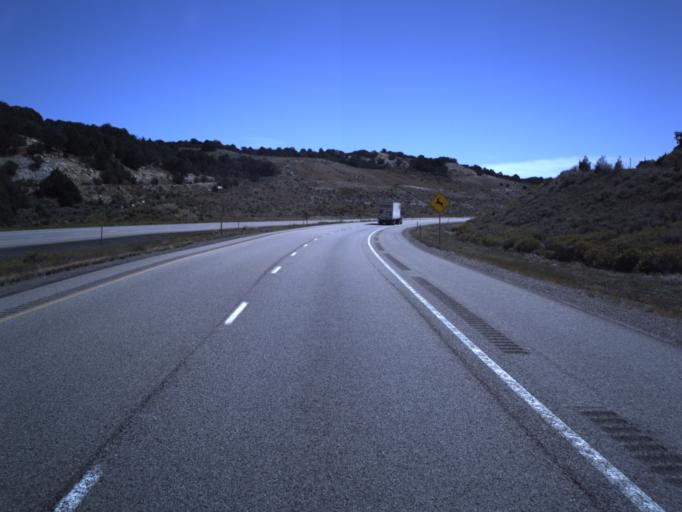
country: US
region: Utah
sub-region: Sevier County
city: Salina
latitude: 38.7832
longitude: -111.4917
